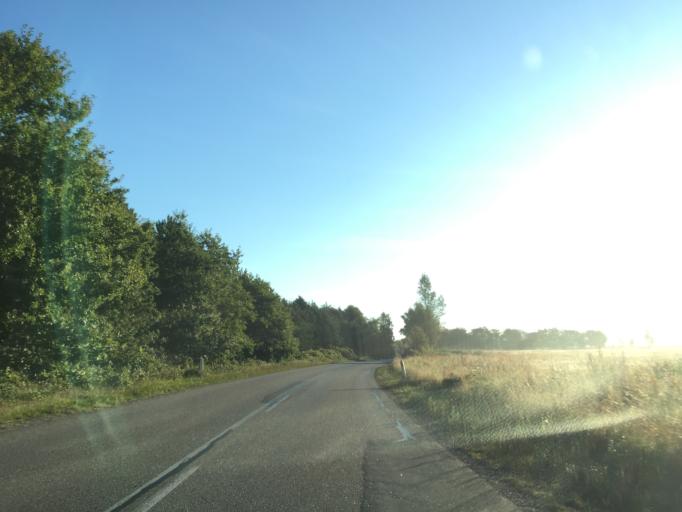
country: DK
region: Central Jutland
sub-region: Viborg Kommune
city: Bjerringbro
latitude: 56.3553
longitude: 9.6639
